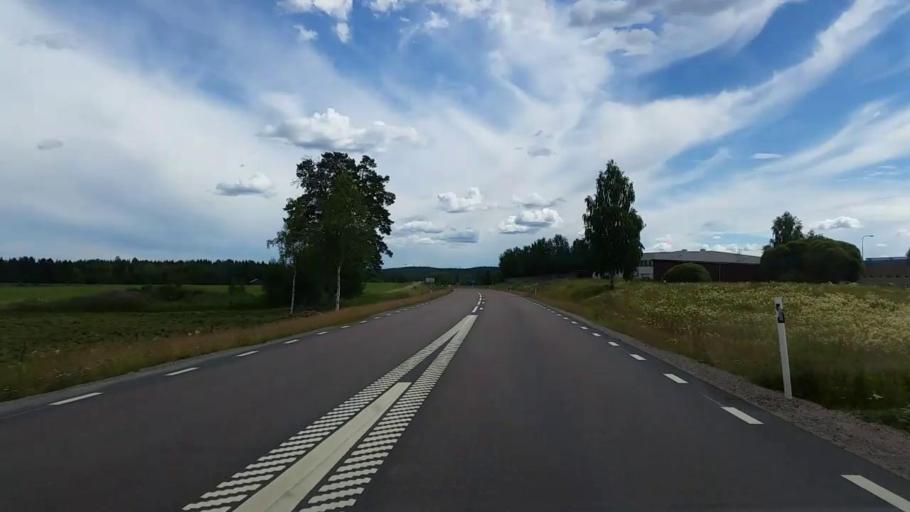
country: SE
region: Gaevleborg
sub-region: Ovanakers Kommun
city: Edsbyn
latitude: 61.3758
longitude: 15.8407
